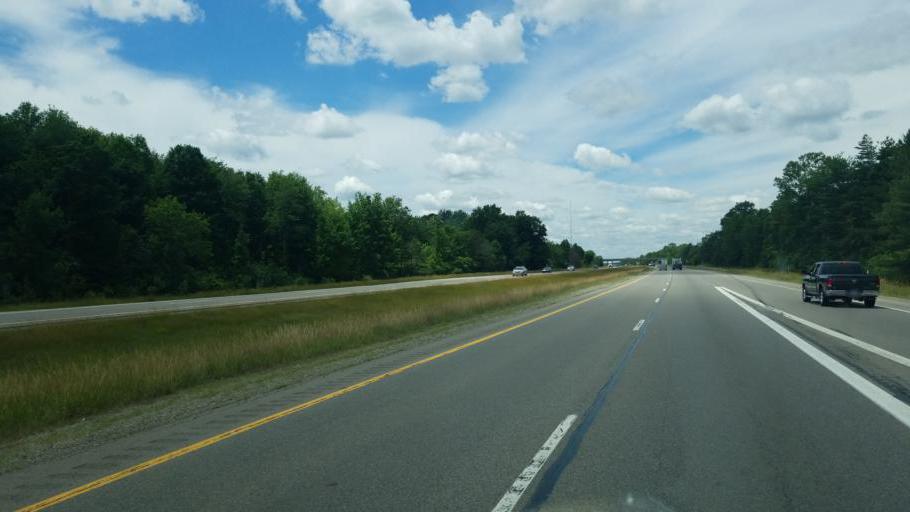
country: US
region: Michigan
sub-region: Eaton County
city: Dimondale
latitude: 42.6654
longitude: -84.5937
